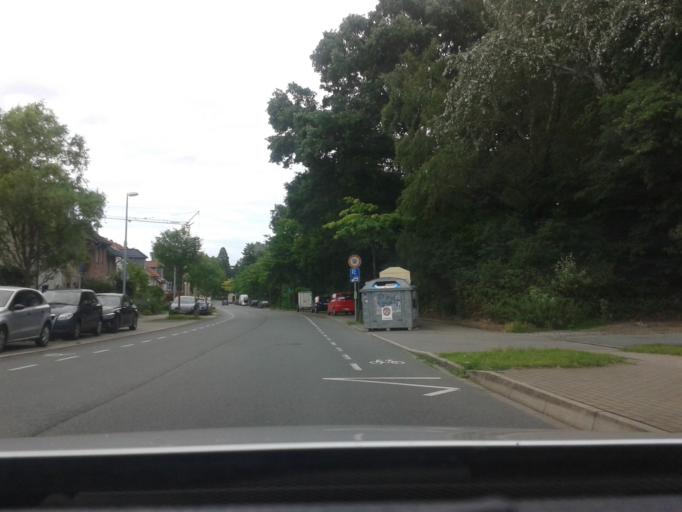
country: DE
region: North Rhine-Westphalia
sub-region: Regierungsbezirk Dusseldorf
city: Muelheim (Ruhr)
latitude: 51.4151
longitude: 6.8418
